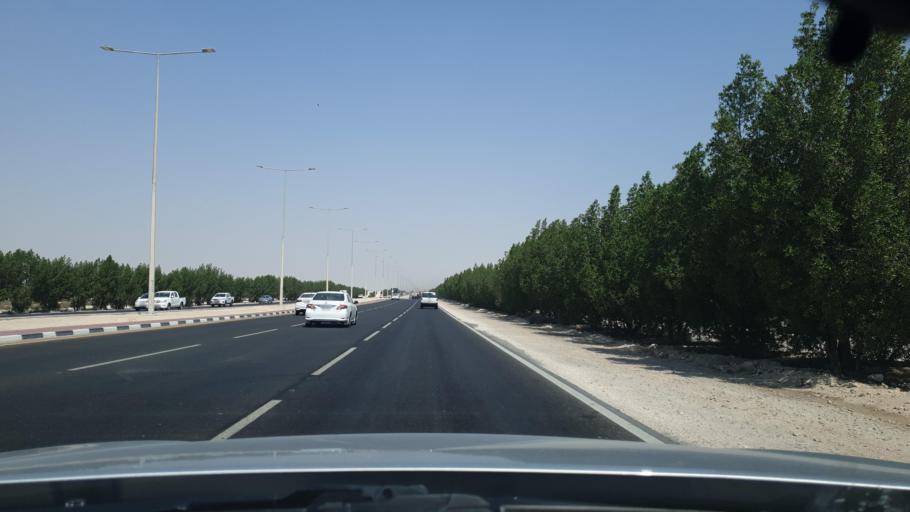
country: QA
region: Al Khawr
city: Al Khawr
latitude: 25.6941
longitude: 51.5015
